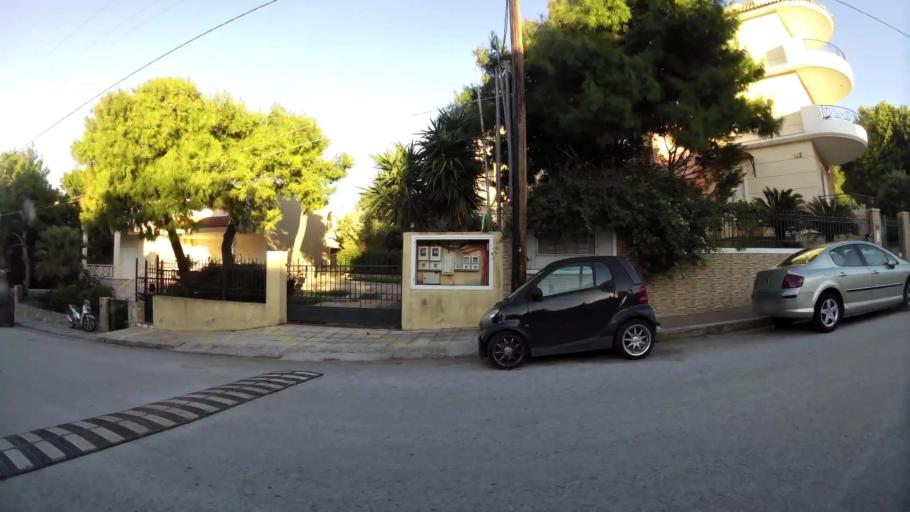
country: GR
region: Attica
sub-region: Nomarchia Anatolikis Attikis
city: Rafina
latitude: 38.0061
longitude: 24.0183
